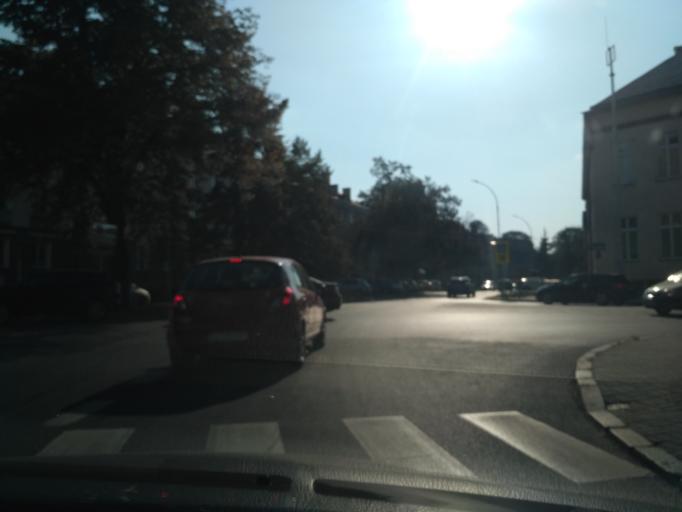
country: PL
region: Subcarpathian Voivodeship
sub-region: Rzeszow
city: Rzeszow
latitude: 50.0336
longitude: 21.9955
